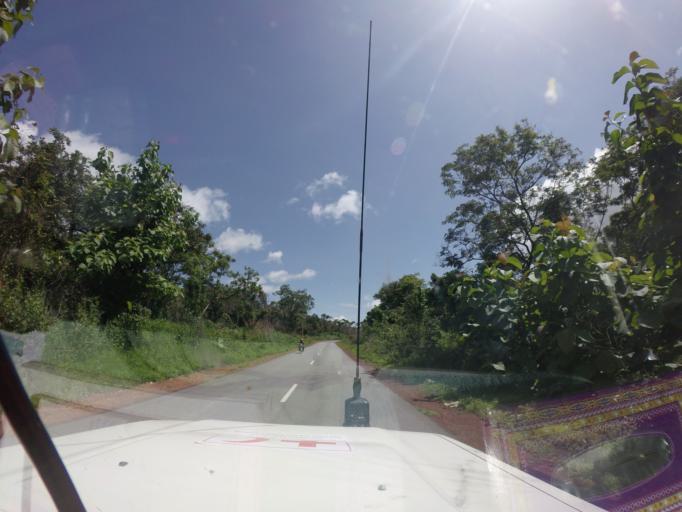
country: GN
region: Mamou
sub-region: Mamou Prefecture
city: Mamou
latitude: 10.1873
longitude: -11.7684
